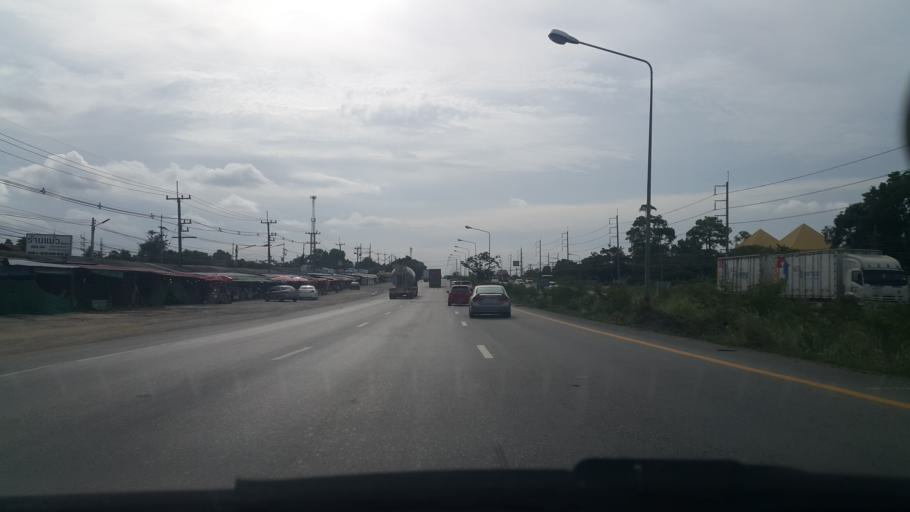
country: TH
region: Rayong
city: Nikhom Phattana
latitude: 12.8635
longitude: 101.0789
